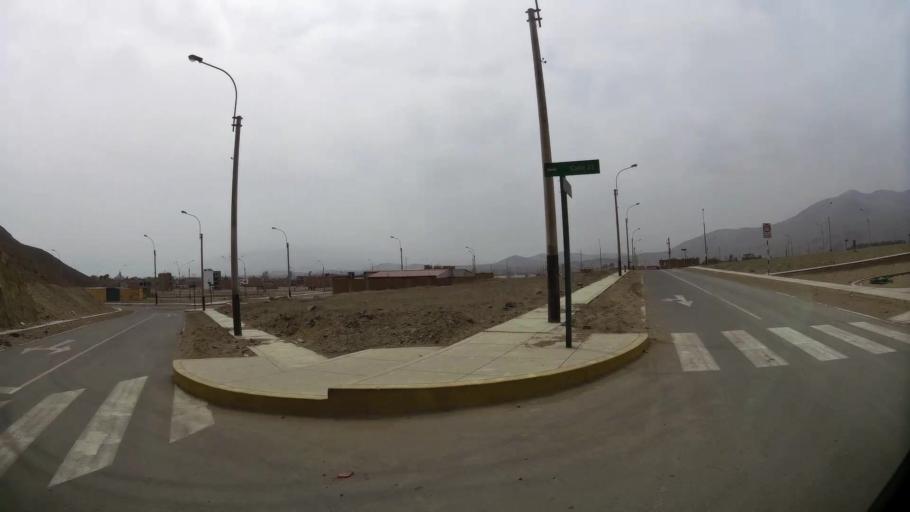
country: PE
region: Lima
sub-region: Lima
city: Santa Rosa
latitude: -11.7949
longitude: -77.1508
